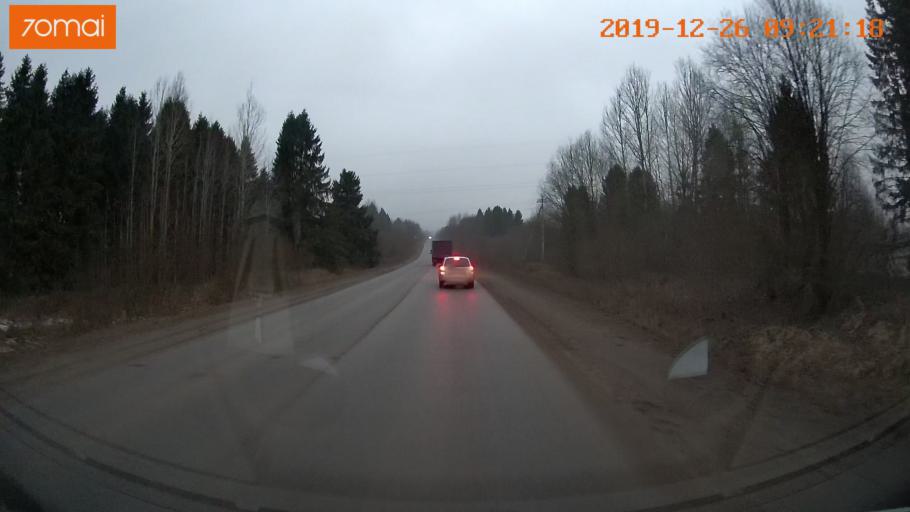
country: RU
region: Vologda
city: Gryazovets
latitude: 58.9694
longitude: 40.2251
